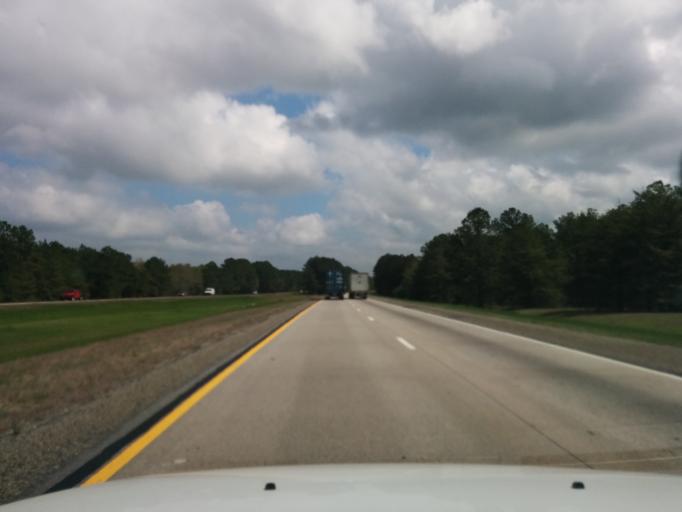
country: US
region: Georgia
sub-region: Bryan County
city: Pembroke
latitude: 32.2280
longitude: -81.5832
